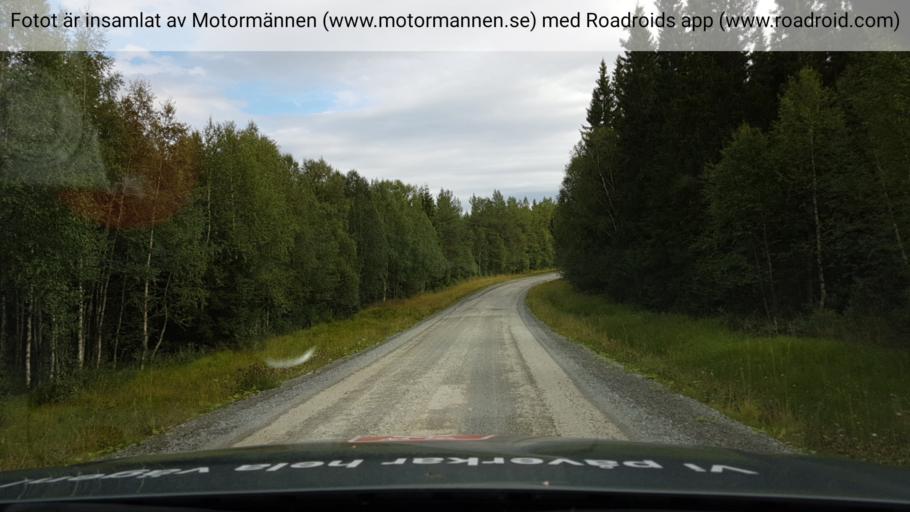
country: SE
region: Jaemtland
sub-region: Krokoms Kommun
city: Valla
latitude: 63.6505
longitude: 13.7838
